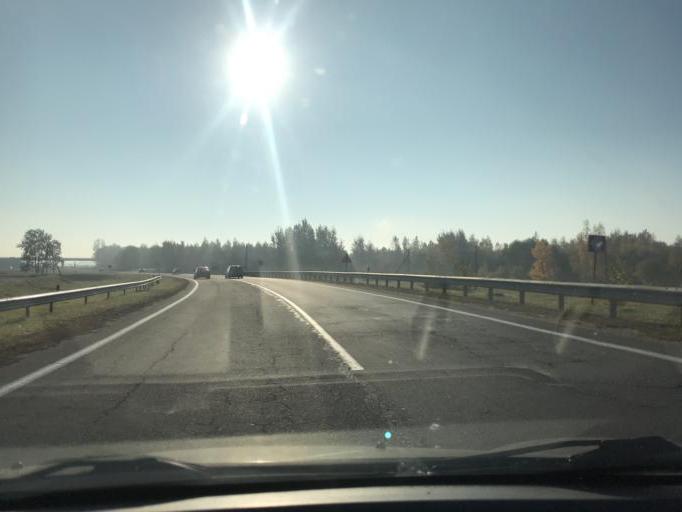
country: BY
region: Minsk
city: Dukora
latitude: 53.6627
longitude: 27.9408
